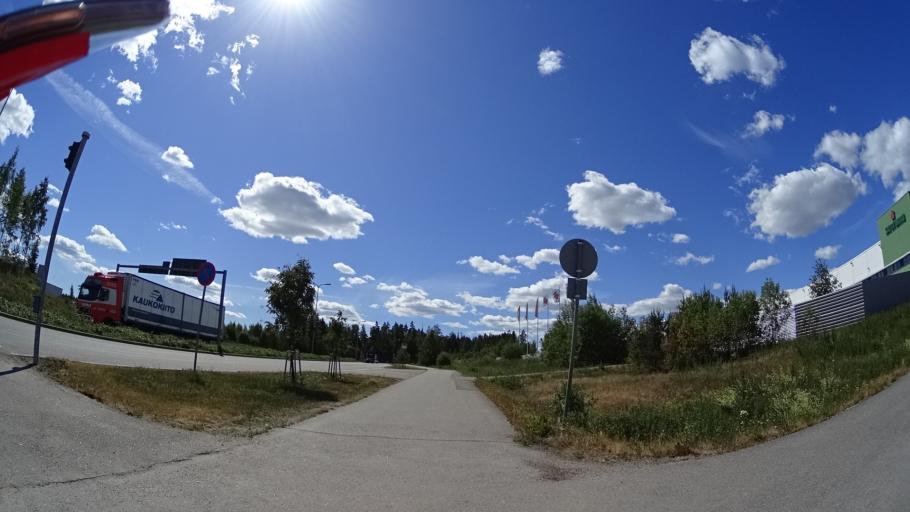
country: FI
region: Uusimaa
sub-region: Helsinki
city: Vantaa
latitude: 60.2963
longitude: 24.9167
